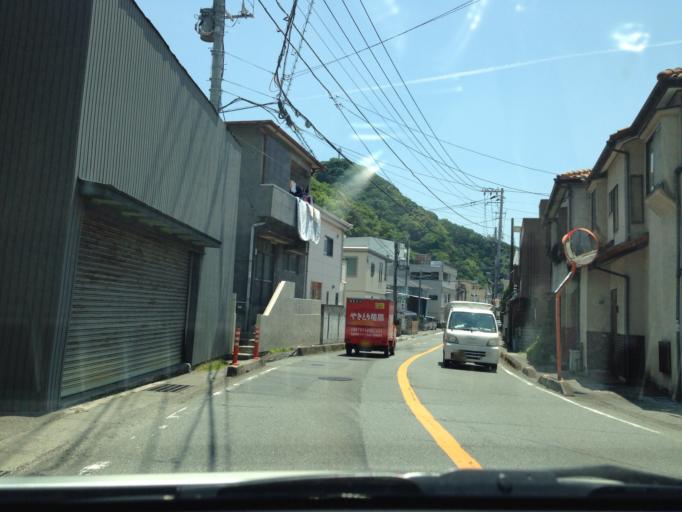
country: JP
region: Shizuoka
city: Numazu
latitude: 35.0568
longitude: 138.8829
